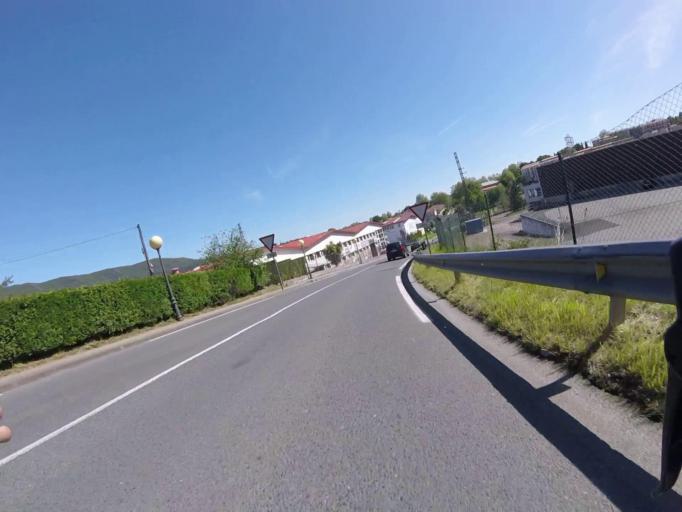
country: ES
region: Basque Country
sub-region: Provincia de Guipuzcoa
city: Irun
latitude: 43.3256
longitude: -1.8229
